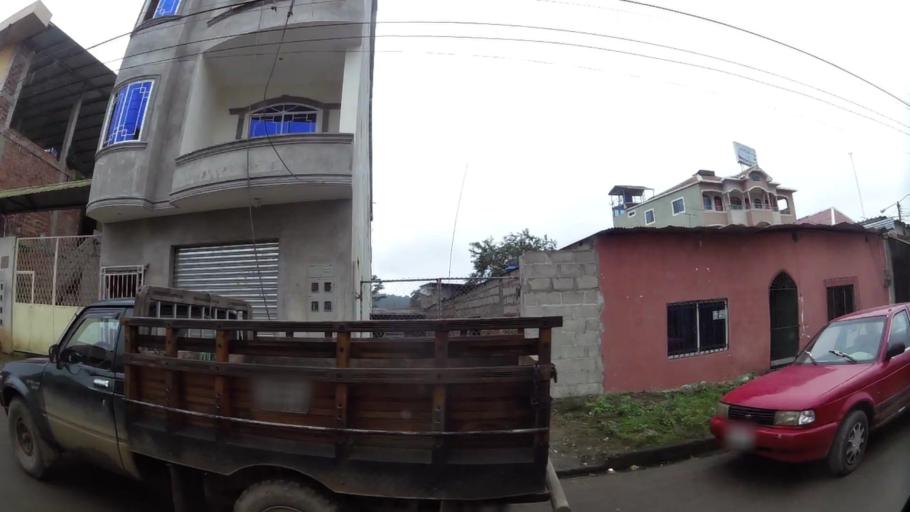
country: EC
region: Guayas
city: Balao
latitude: -3.0627
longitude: -79.7448
